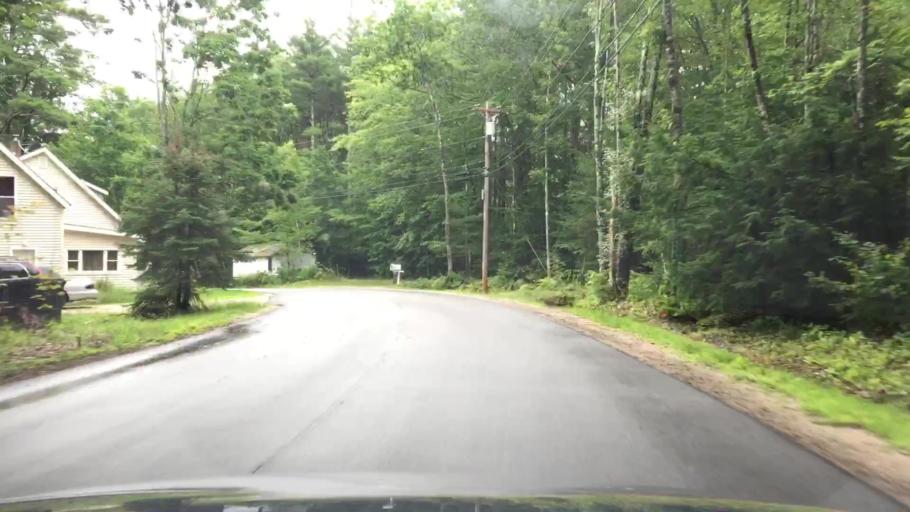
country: US
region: New Hampshire
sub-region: Carroll County
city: Center Harbor
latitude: 43.7263
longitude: -71.4823
